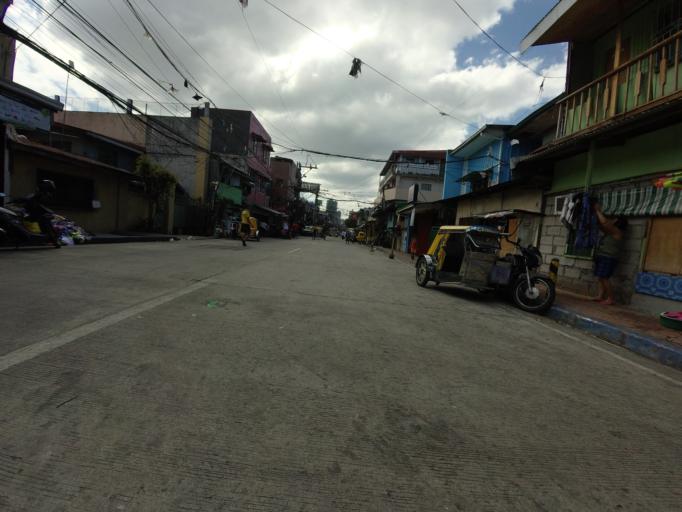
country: PH
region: Metro Manila
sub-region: City of Manila
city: Quiapo
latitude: 14.5738
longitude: 121.0061
